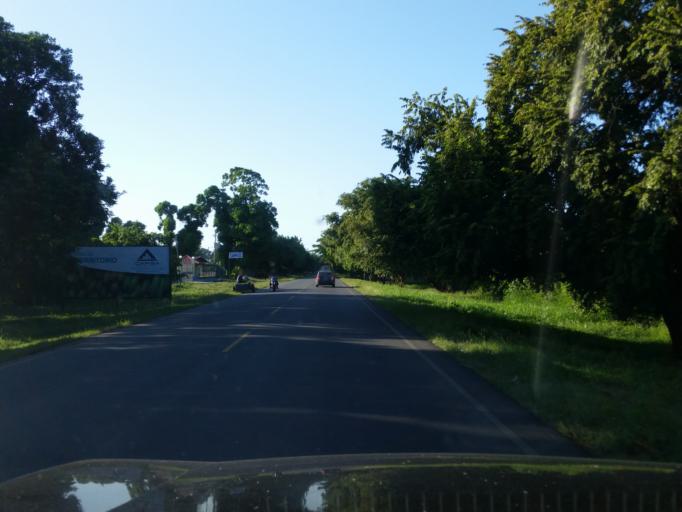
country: NI
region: Rivas
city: Potosi
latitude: 11.4703
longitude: -85.8571
